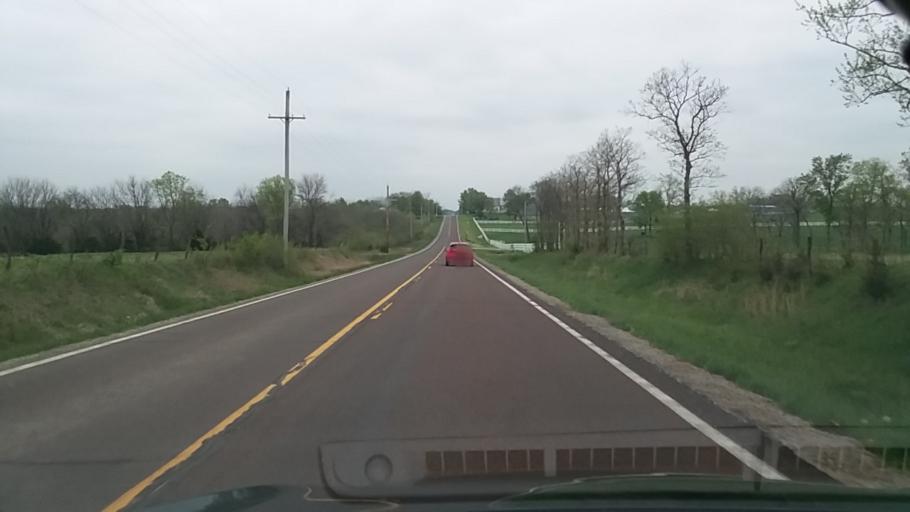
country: US
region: Kansas
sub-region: Johnson County
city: Edgerton
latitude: 38.8305
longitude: -95.0932
